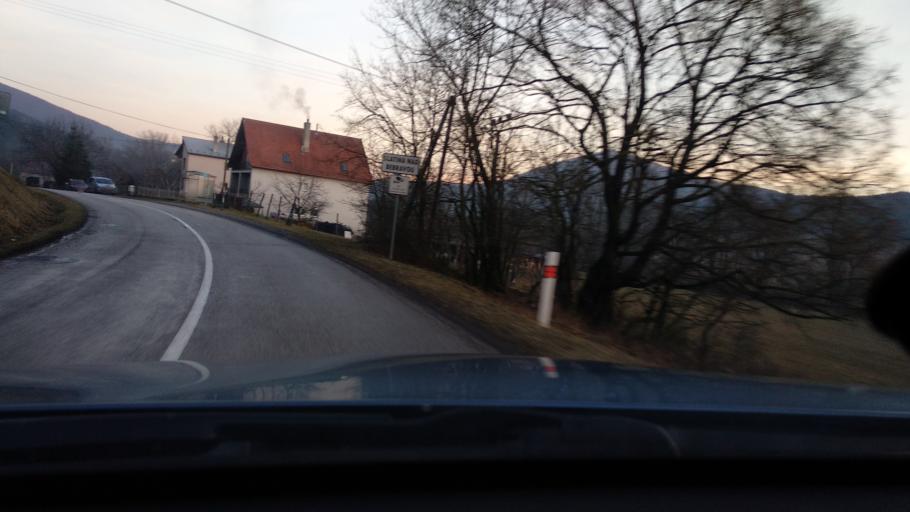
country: SK
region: Nitriansky
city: Trencianske Teplice
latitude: 48.8421
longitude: 18.2515
